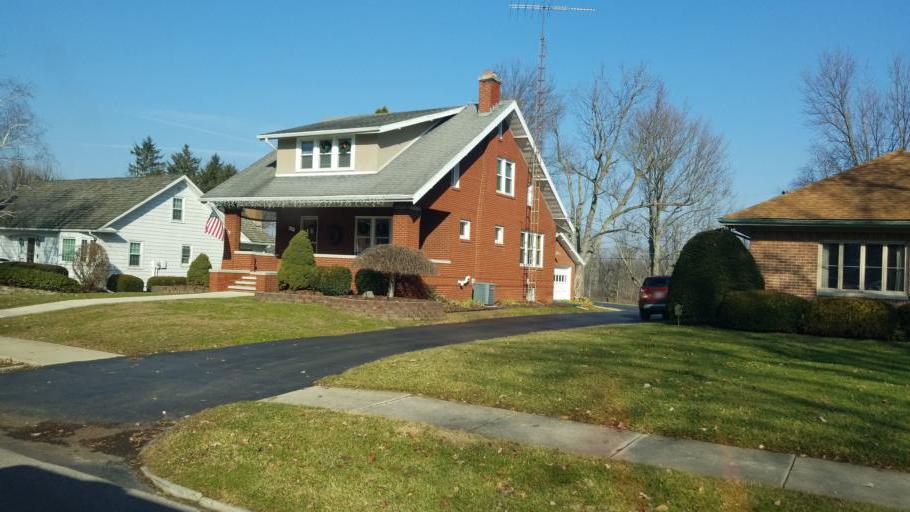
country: US
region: Ohio
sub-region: Seneca County
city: Tiffin
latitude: 41.1043
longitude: -83.1638
